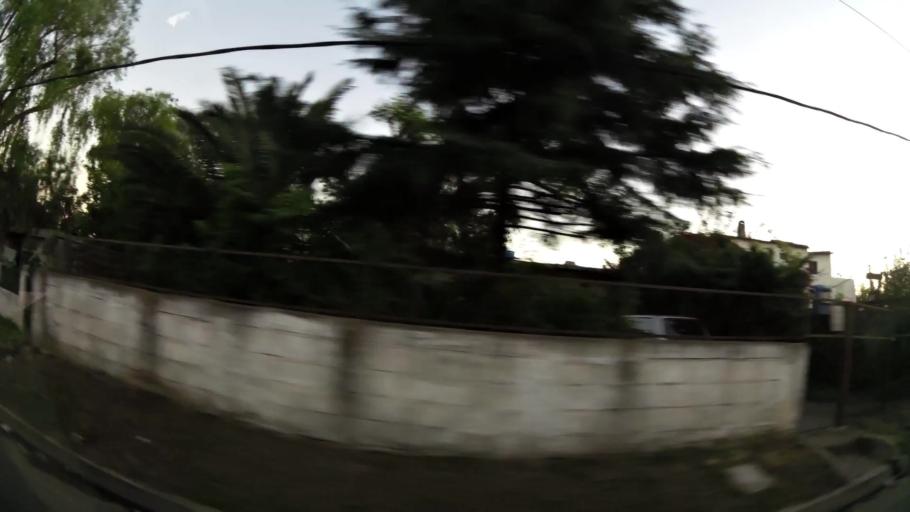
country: UY
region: Canelones
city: Toledo
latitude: -34.8180
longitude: -56.1499
